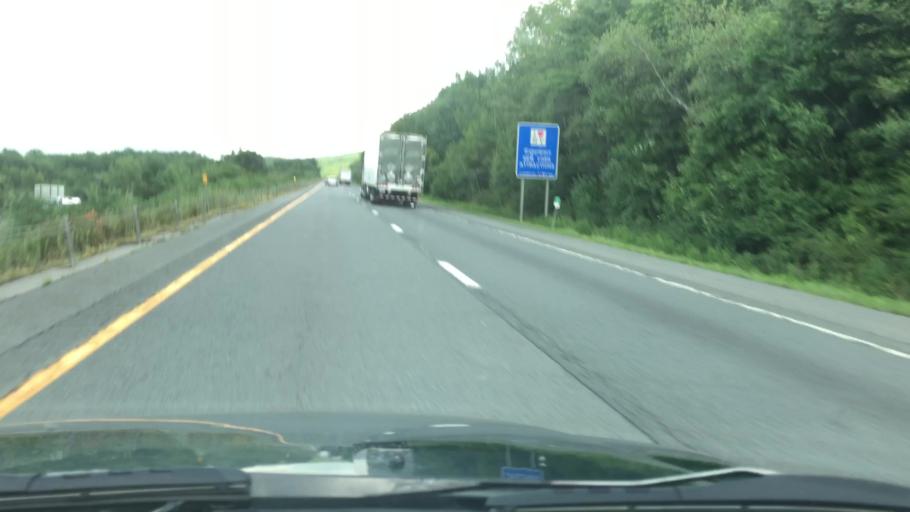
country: US
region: New York
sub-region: Orange County
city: Port Jervis
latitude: 41.3548
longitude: -74.6732
